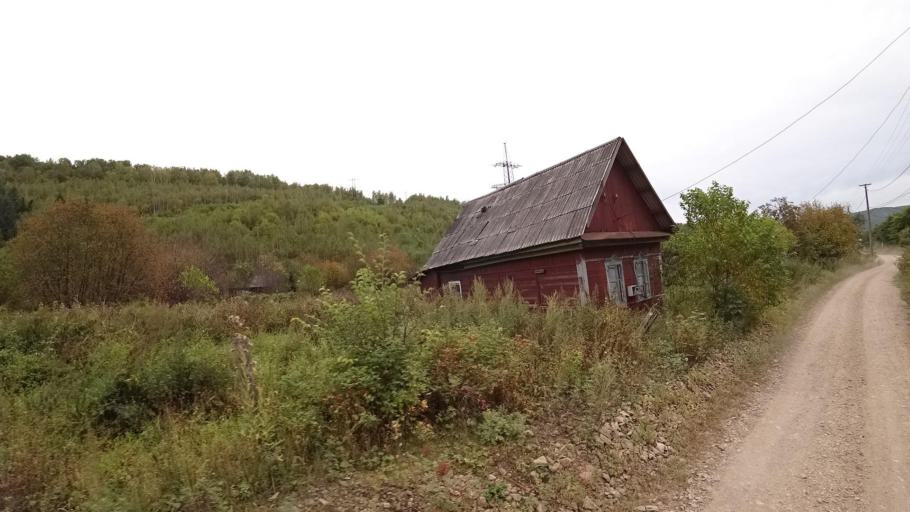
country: RU
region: Jewish Autonomous Oblast
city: Khingansk
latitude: 49.0254
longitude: 131.0729
